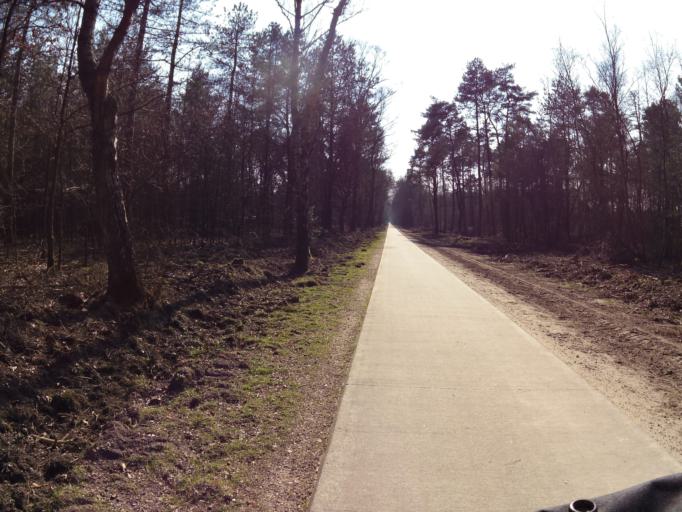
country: NL
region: Gelderland
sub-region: Gemeente Epe
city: Epe
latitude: 52.3693
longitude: 5.9565
